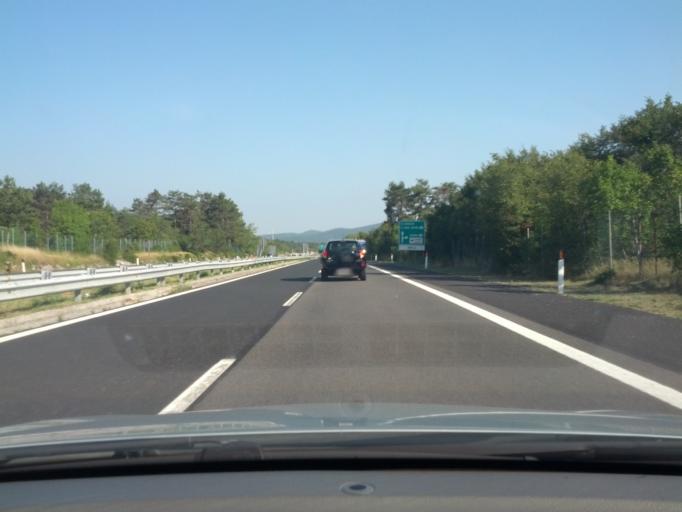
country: IT
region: Friuli Venezia Giulia
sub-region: Provincia di Trieste
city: Villa Opicina
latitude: 45.6828
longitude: 13.8142
